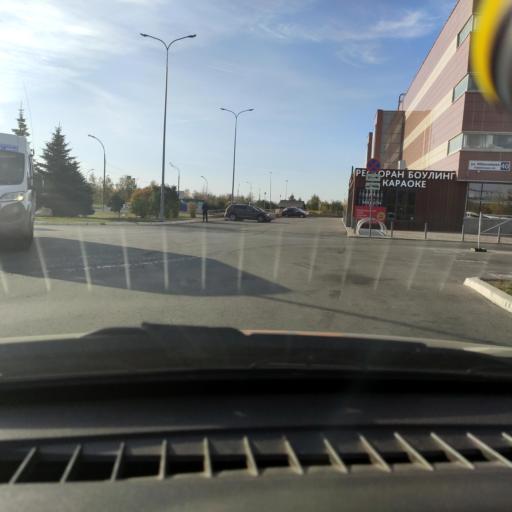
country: RU
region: Samara
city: Tol'yatti
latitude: 53.5018
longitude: 49.2740
